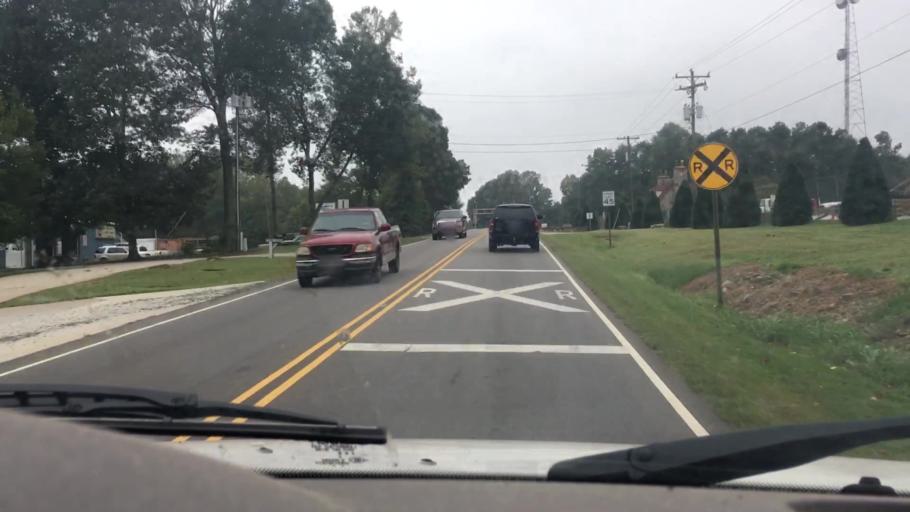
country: US
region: North Carolina
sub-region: Iredell County
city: Mooresville
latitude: 35.6074
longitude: -80.8032
